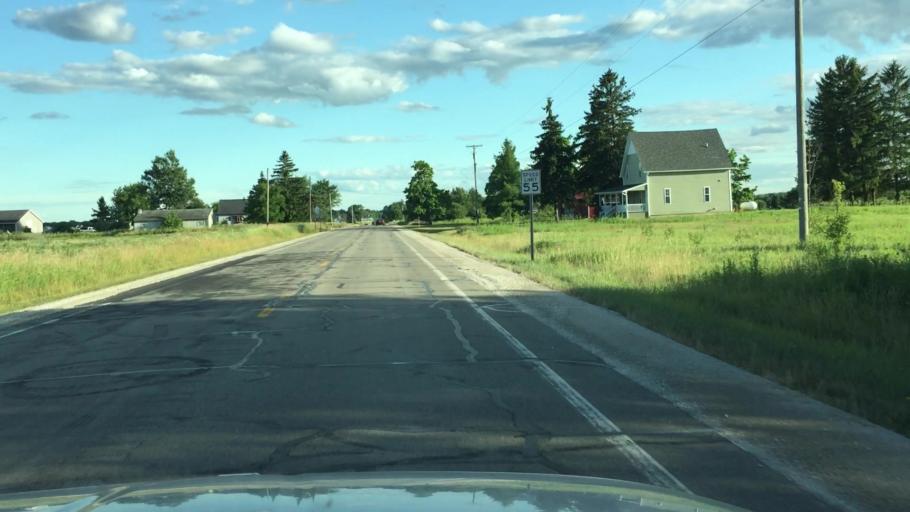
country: US
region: Michigan
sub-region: Saint Clair County
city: Yale
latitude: 43.0866
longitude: -82.7660
